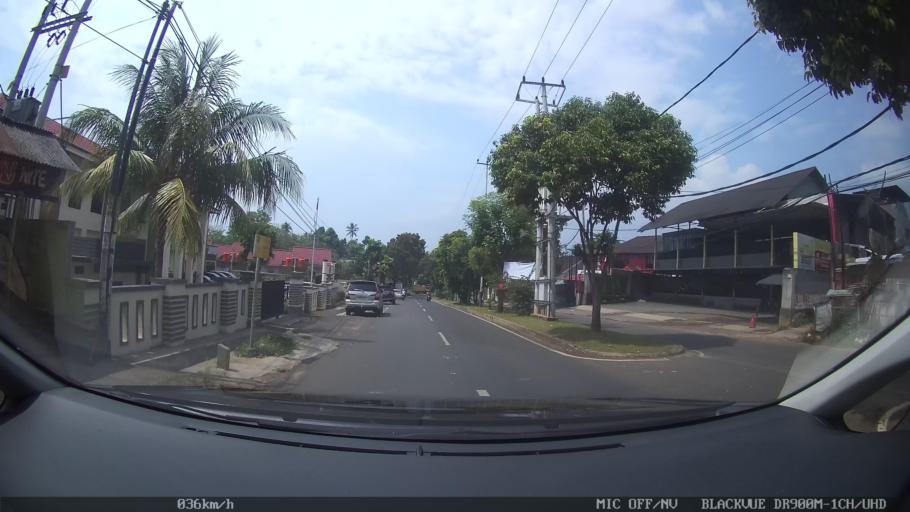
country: ID
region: Lampung
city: Bandarlampung
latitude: -5.4244
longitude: 105.2472
